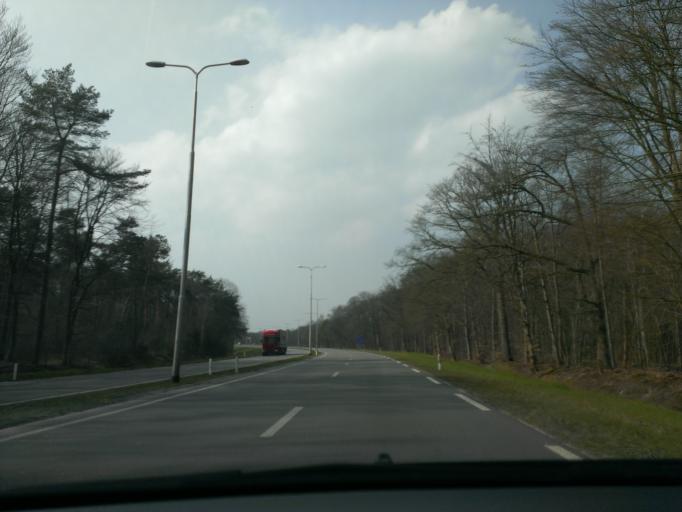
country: NL
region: Gelderland
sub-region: Gemeente Apeldoorn
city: Apeldoorn
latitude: 52.2050
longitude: 6.0300
